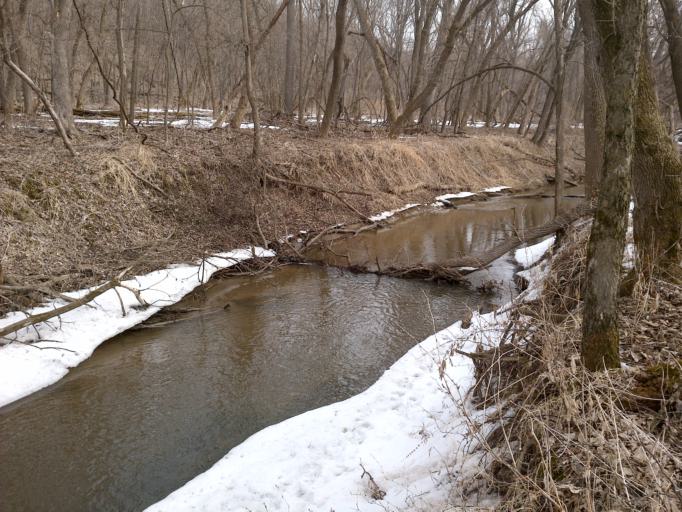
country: US
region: Minnesota
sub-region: Wabasha County
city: Lake City
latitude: 44.4516
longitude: -92.2984
